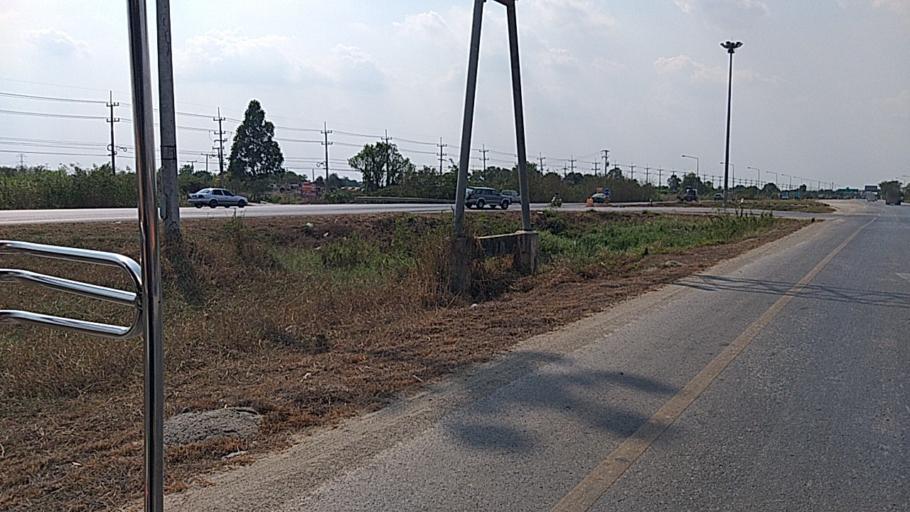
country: TH
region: Pathum Thani
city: Sam Khok
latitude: 14.0985
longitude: 100.5154
